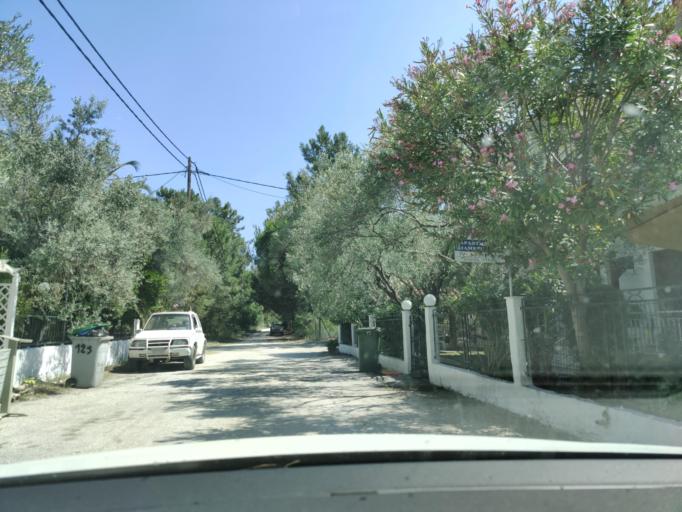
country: GR
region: East Macedonia and Thrace
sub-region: Nomos Kavalas
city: Prinos
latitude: 40.7584
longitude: 24.5623
